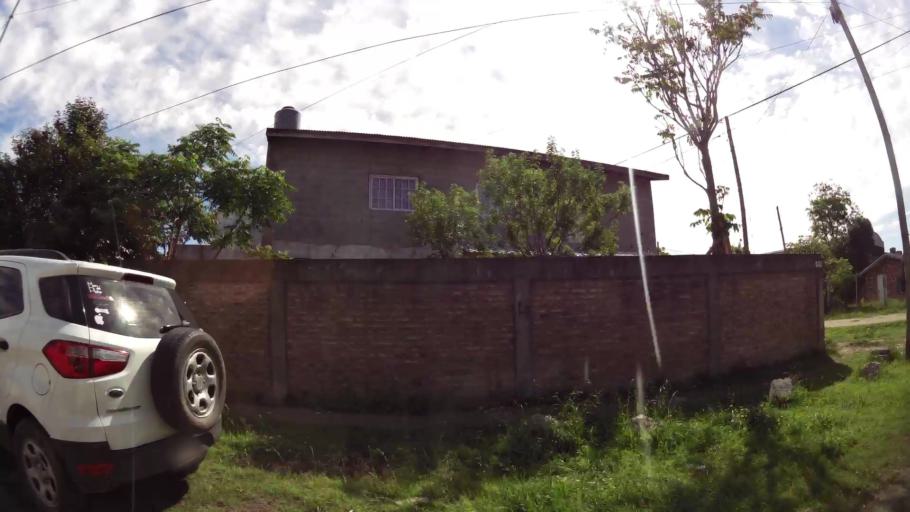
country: AR
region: Buenos Aires
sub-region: Partido de Quilmes
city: Quilmes
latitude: -34.7708
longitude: -58.2900
